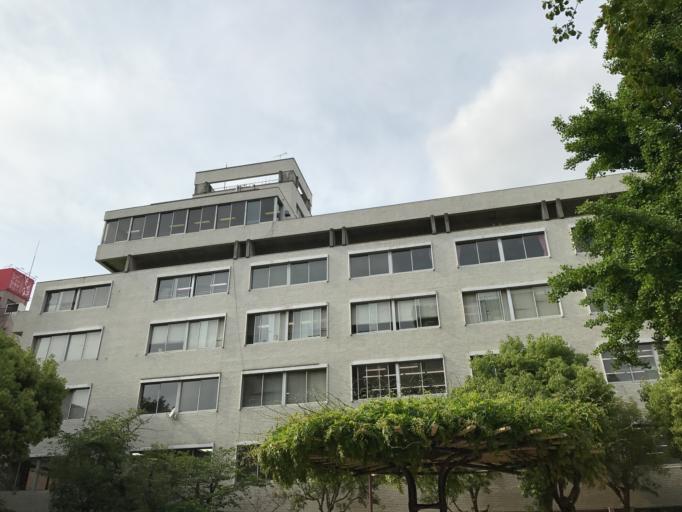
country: JP
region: Nagasaki
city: Nagasaki-shi
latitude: 32.7498
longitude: 129.8733
